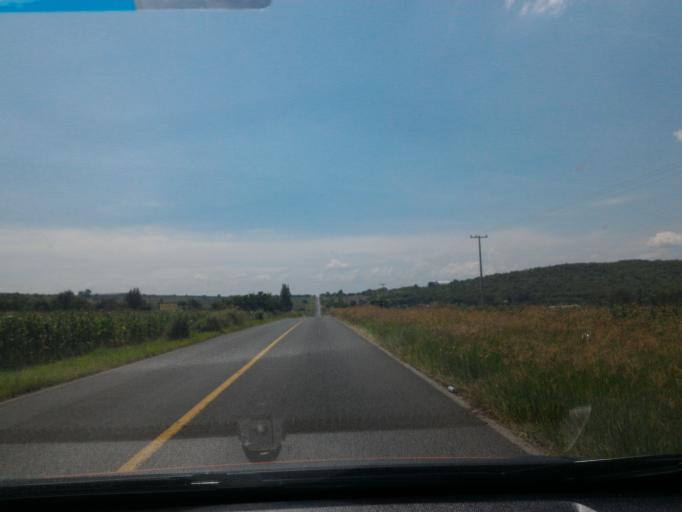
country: MX
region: Guanajuato
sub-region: Penjamo
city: Estacion la Piedad
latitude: 20.4424
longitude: -101.9862
